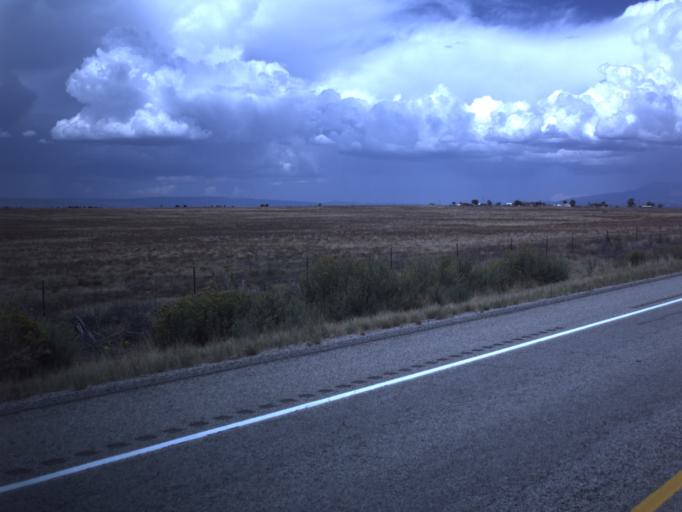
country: US
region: Utah
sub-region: San Juan County
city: Blanding
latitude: 37.4462
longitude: -109.4673
